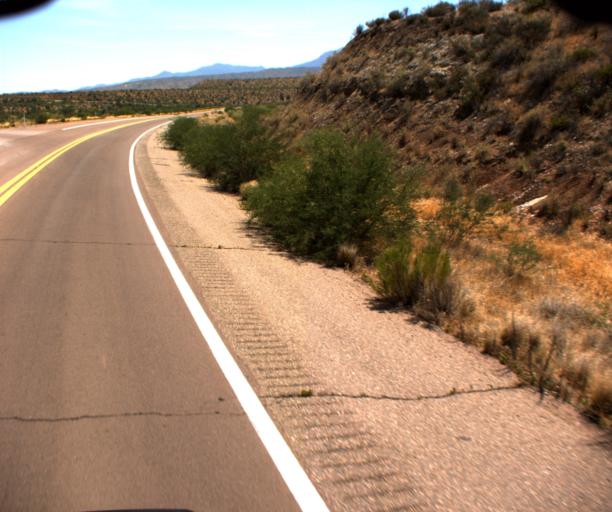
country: US
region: Arizona
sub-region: Gila County
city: Tonto Basin
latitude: 33.8178
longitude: -111.2886
